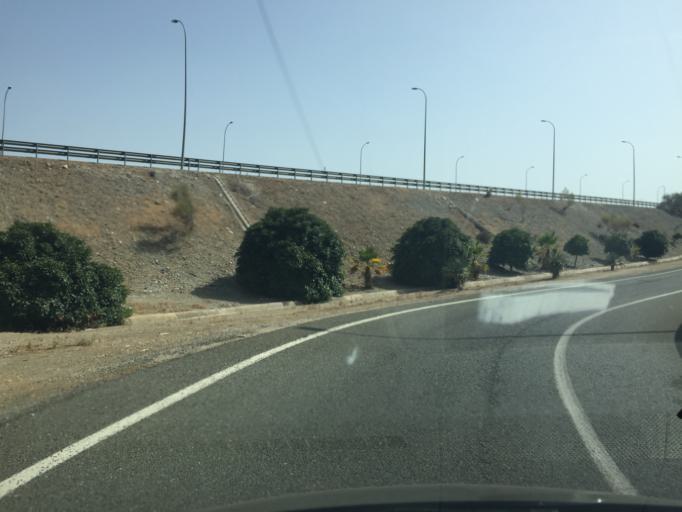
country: ES
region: Andalusia
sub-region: Provincia de Granada
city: La Herradura
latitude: 36.7524
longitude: -3.7519
